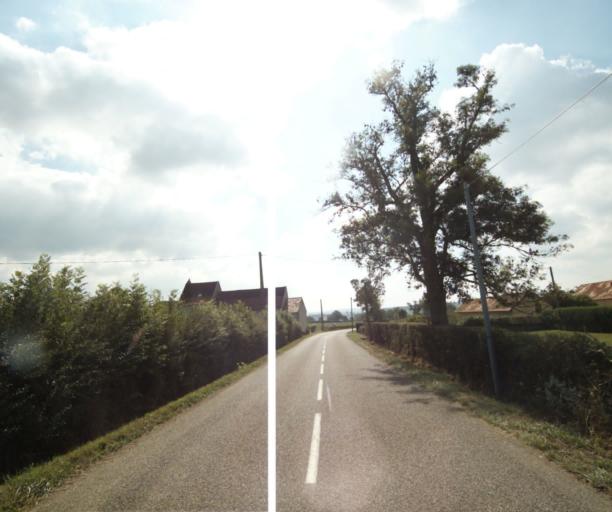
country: FR
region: Bourgogne
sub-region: Departement de Saone-et-Loire
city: Charolles
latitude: 46.3752
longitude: 4.2482
